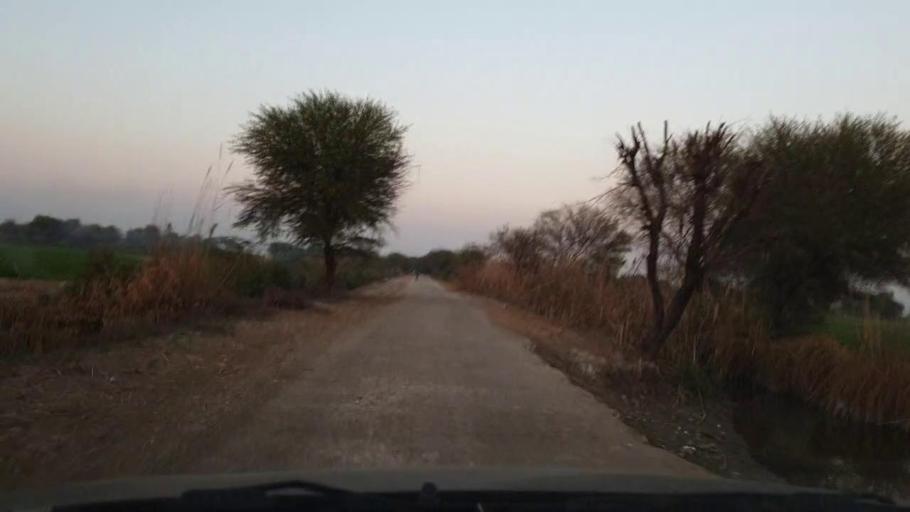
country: PK
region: Sindh
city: Jhol
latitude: 25.9386
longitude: 68.9714
